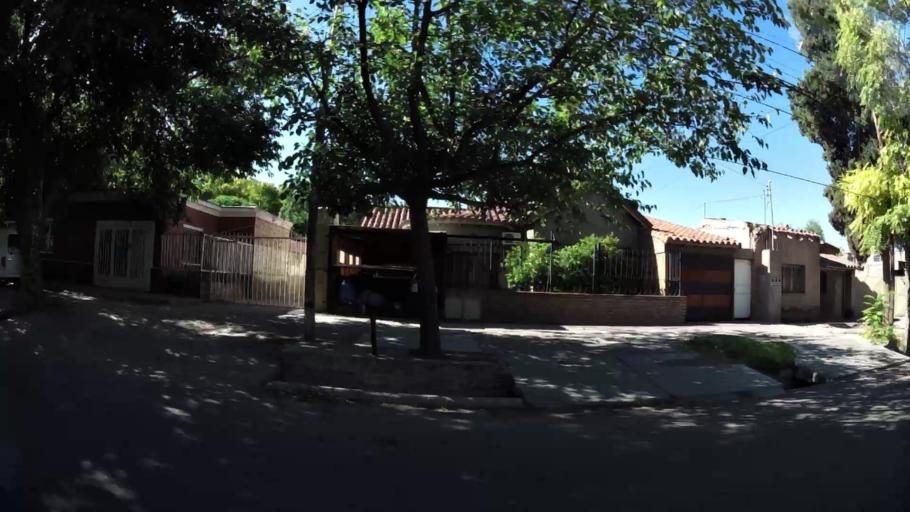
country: AR
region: Mendoza
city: Las Heras
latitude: -32.8420
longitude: -68.8259
